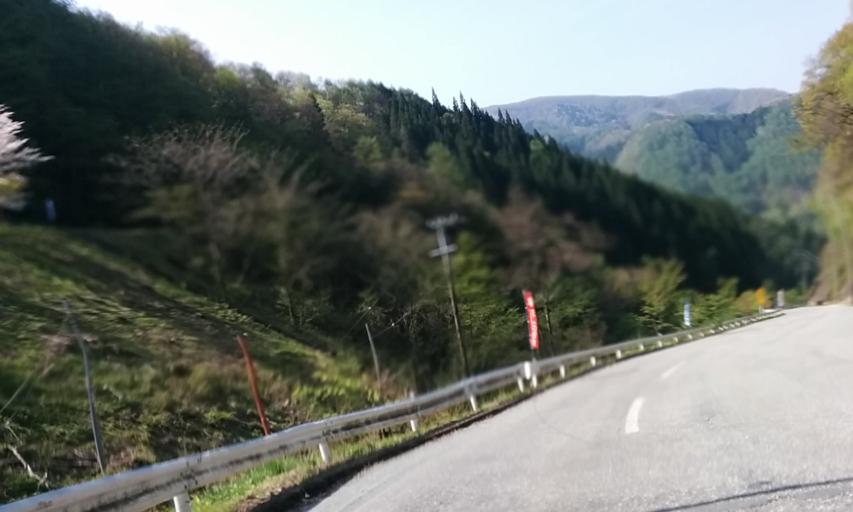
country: JP
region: Gifu
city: Takayama
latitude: 36.1833
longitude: 137.4241
